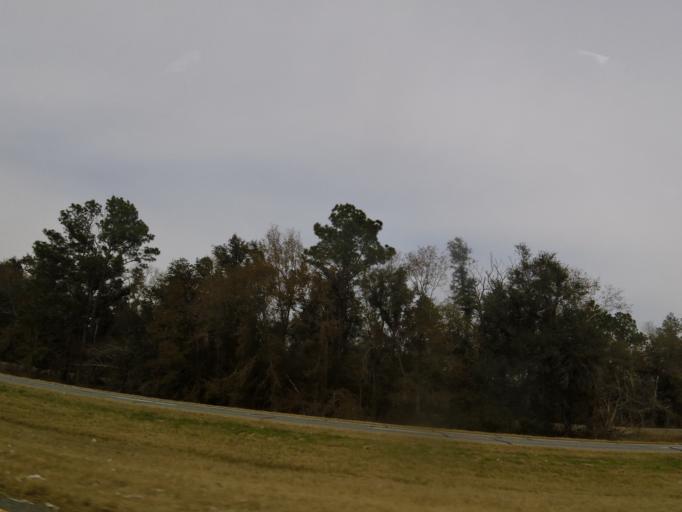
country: US
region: Georgia
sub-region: Seminole County
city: Donalsonville
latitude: 31.0229
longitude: -84.8356
